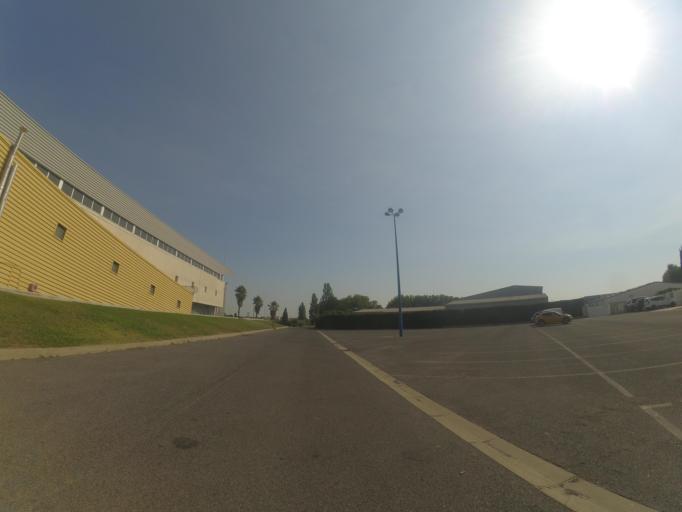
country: FR
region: Languedoc-Roussillon
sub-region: Departement des Pyrenees-Orientales
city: Canohes
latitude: 42.6624
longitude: 2.8341
